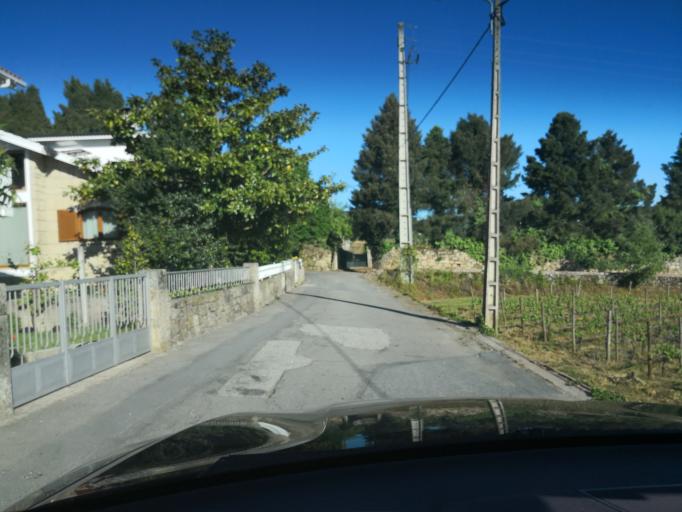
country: PT
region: Vila Real
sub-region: Vila Real
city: Vila Real
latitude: 41.2964
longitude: -7.7151
